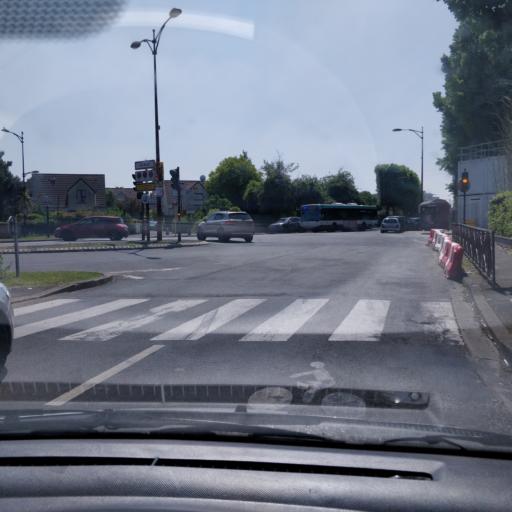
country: FR
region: Ile-de-France
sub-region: Departement de Seine-Saint-Denis
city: Bondy
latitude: 48.9177
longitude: 2.4848
